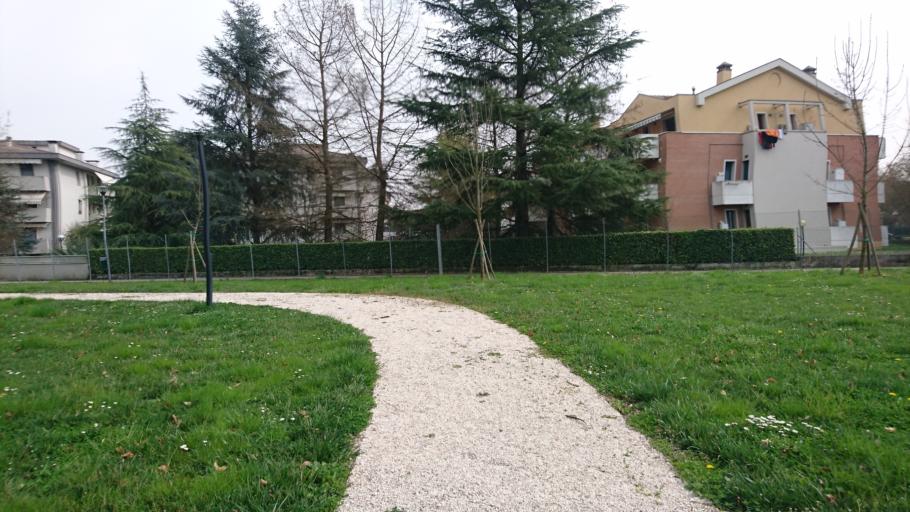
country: IT
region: Veneto
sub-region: Provincia di Padova
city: Selvazzano Dentro
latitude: 45.3913
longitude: 11.7839
